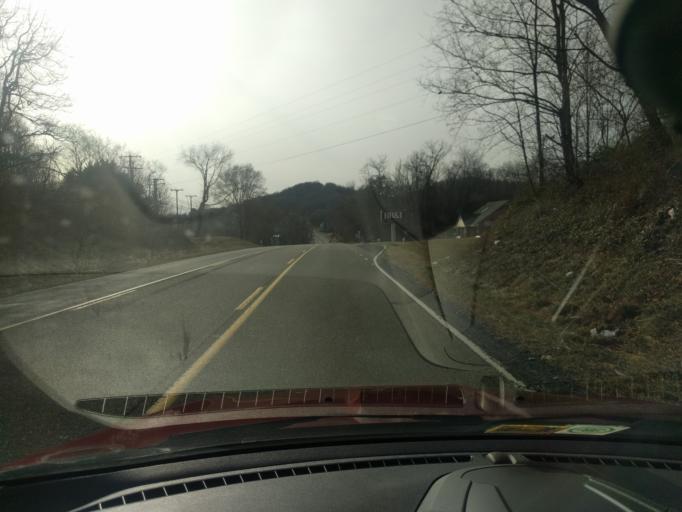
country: US
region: Virginia
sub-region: Augusta County
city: Stuarts Draft
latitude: 38.0072
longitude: -79.1534
